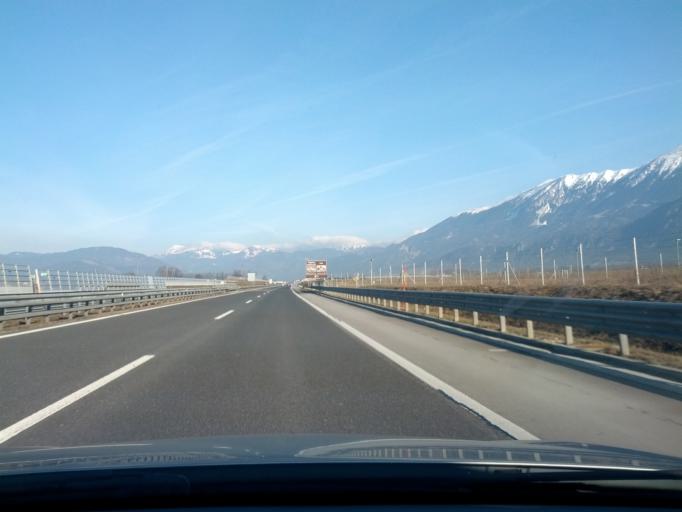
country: SI
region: Radovljica
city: Radovljica
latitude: 46.3477
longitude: 14.1812
